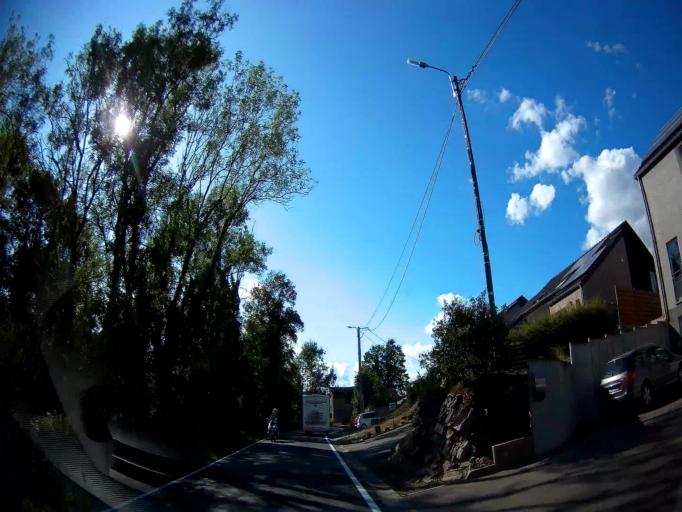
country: BE
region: Wallonia
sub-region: Province de Namur
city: Mettet
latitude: 50.3161
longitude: 4.7574
